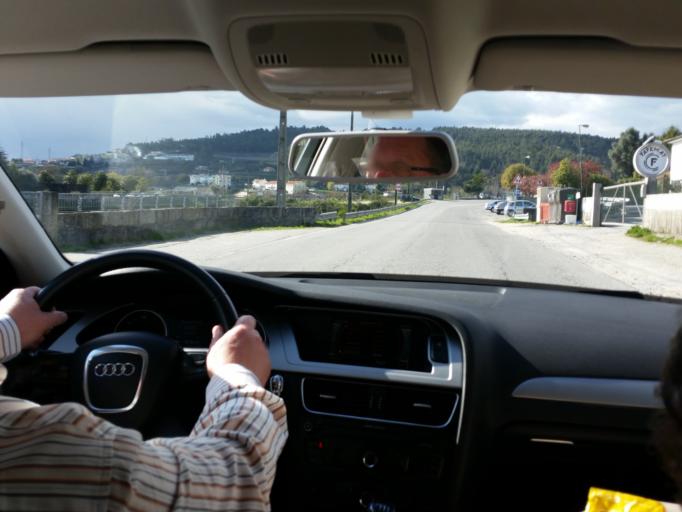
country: PT
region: Braga
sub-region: Fafe
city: Aroes
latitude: 41.4548
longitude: -8.2163
